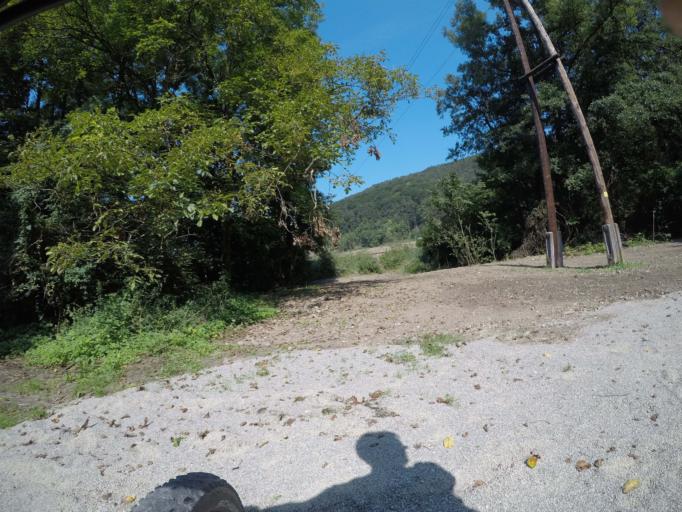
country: AT
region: Lower Austria
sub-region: Politischer Bezirk Baden
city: Pottenstein
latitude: 47.9672
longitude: 16.0800
